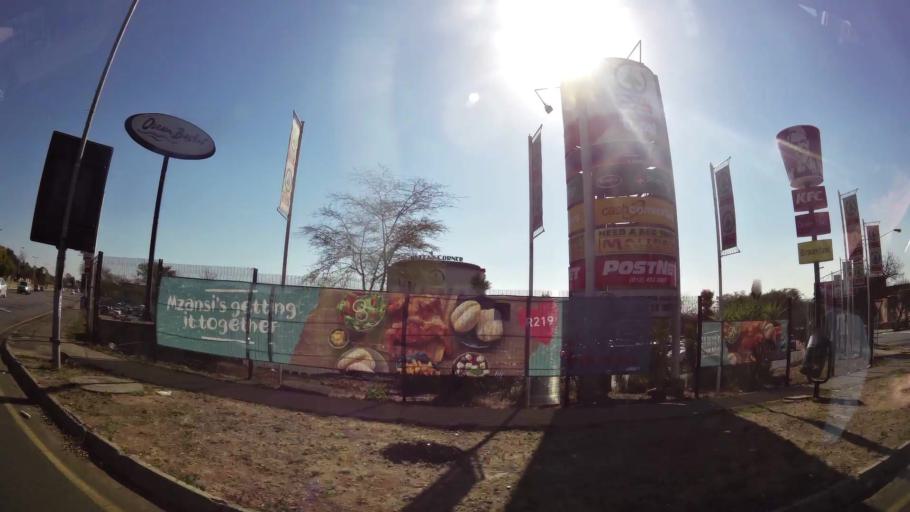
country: ZA
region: Gauteng
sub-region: City of Tshwane Metropolitan Municipality
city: Pretoria
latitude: -25.7327
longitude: 28.2459
